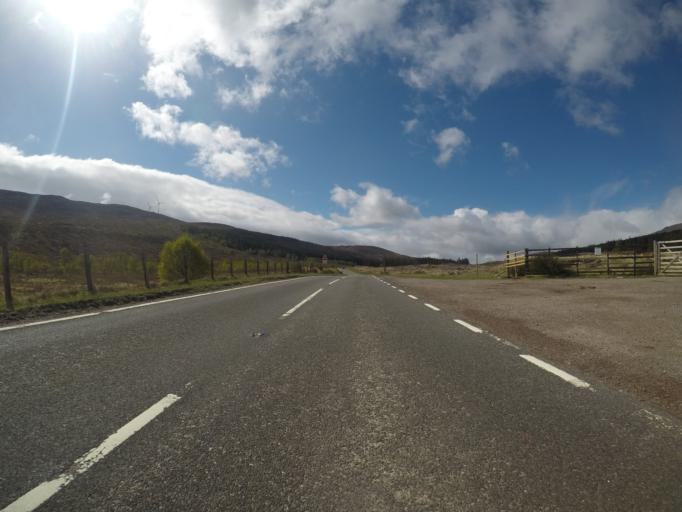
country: GB
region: Scotland
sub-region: Highland
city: Spean Bridge
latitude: 57.1378
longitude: -4.9540
